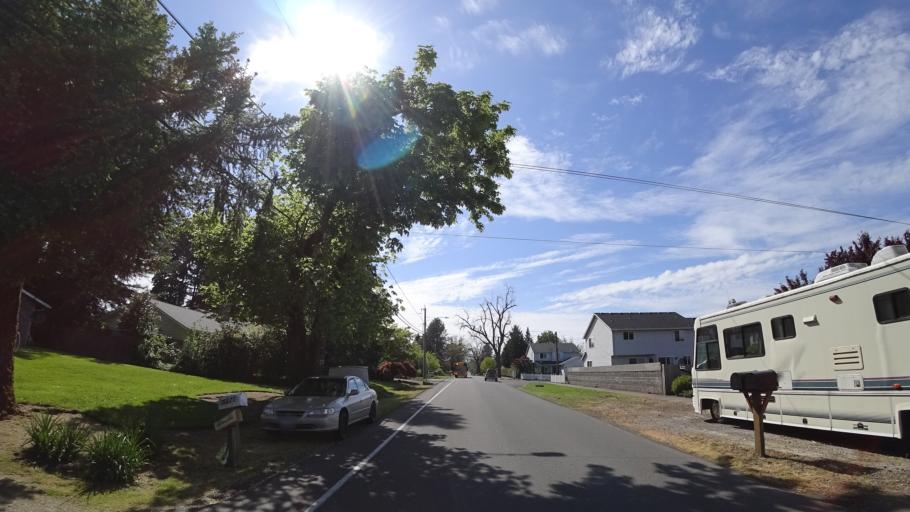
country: US
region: Oregon
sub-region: Washington County
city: Aloha
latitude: 45.5005
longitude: -122.8836
